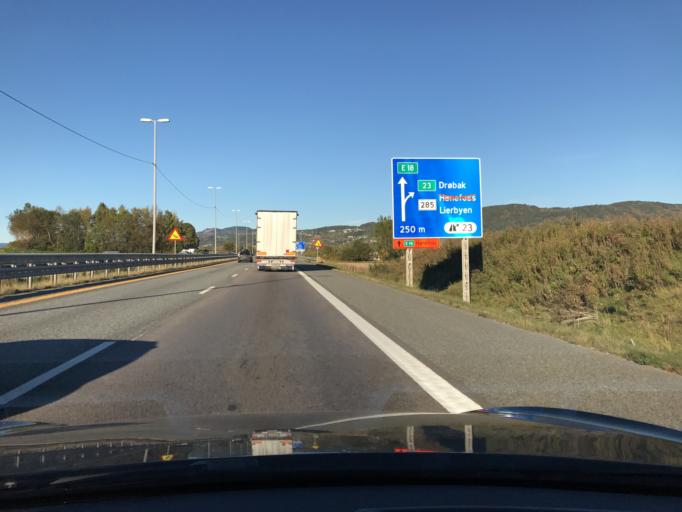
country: NO
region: Buskerud
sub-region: Lier
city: Lierbyen
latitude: 59.7590
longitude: 10.2509
